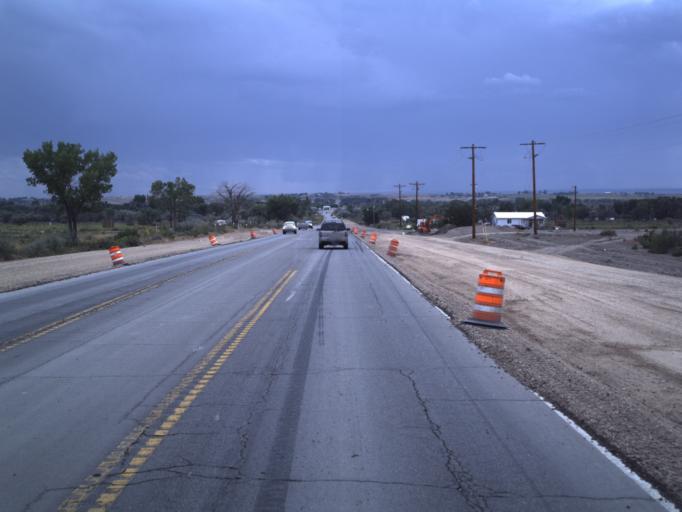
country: US
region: Utah
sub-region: Duchesne County
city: Roosevelt
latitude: 40.2133
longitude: -110.0675
